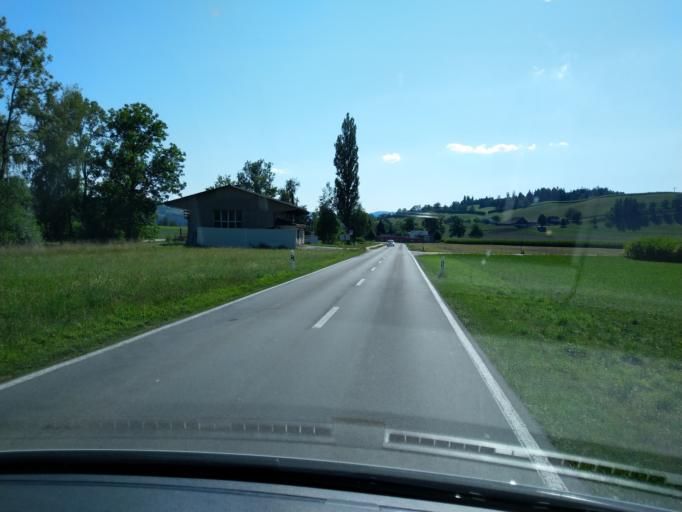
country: CH
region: Lucerne
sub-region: Sursee District
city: Ruswil
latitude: 47.0793
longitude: 8.1121
